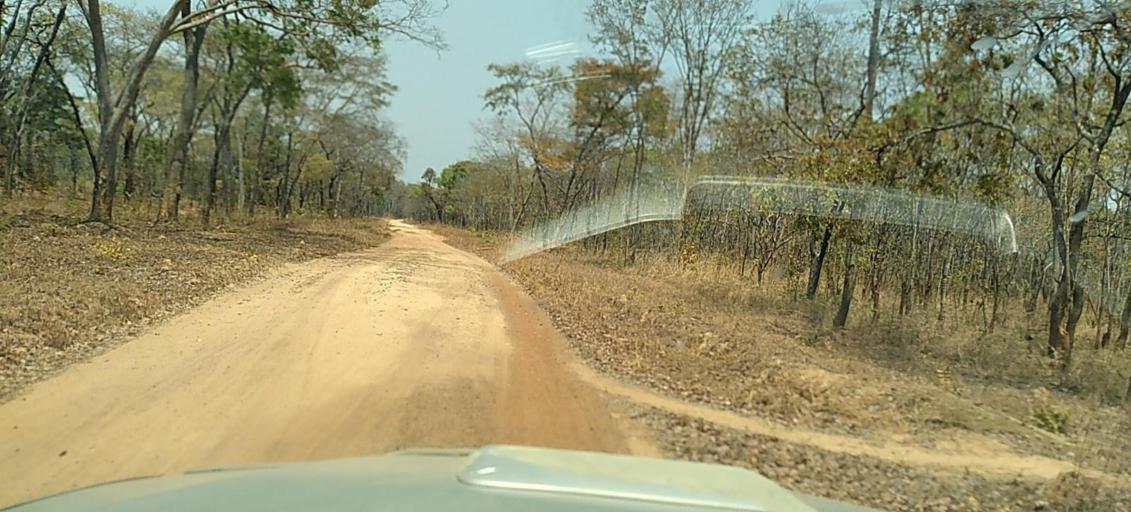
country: ZM
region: North-Western
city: Kasempa
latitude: -13.6127
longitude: 26.1972
